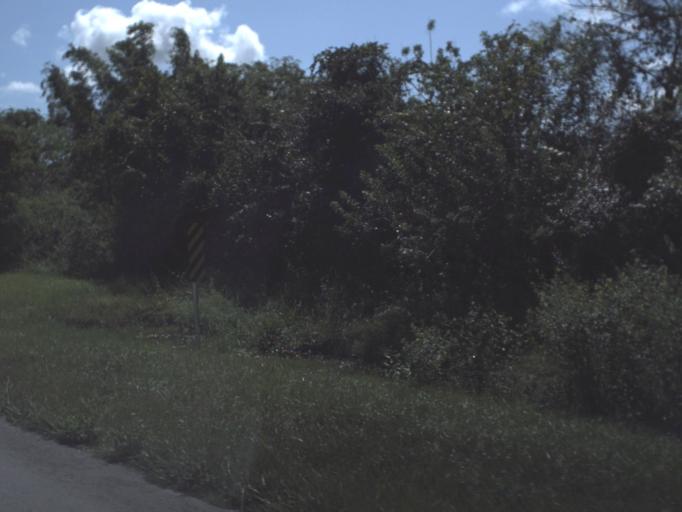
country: US
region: Florida
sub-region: Sarasota County
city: The Meadows
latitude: 27.4752
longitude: -82.3438
